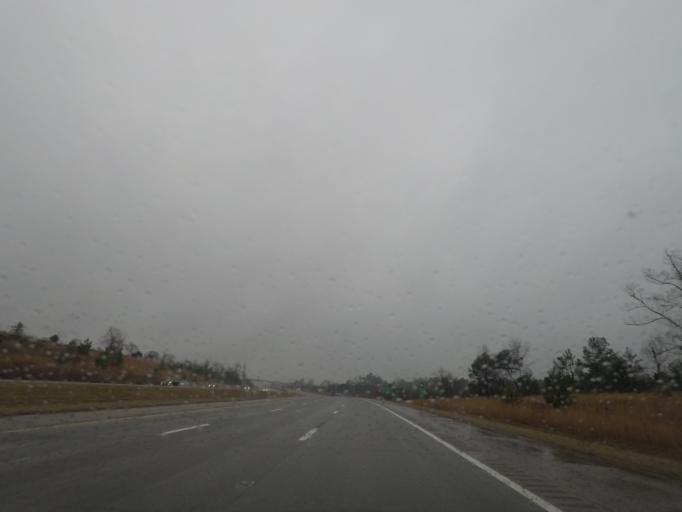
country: US
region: North Carolina
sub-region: Wake County
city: Green Level
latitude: 35.7602
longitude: -78.8909
